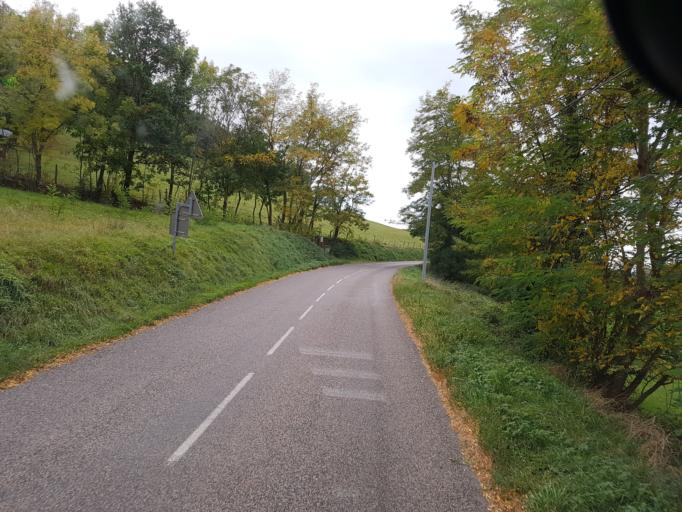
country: FR
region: Rhone-Alpes
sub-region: Departement du Rhone
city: Aveize
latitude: 45.6882
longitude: 4.4565
